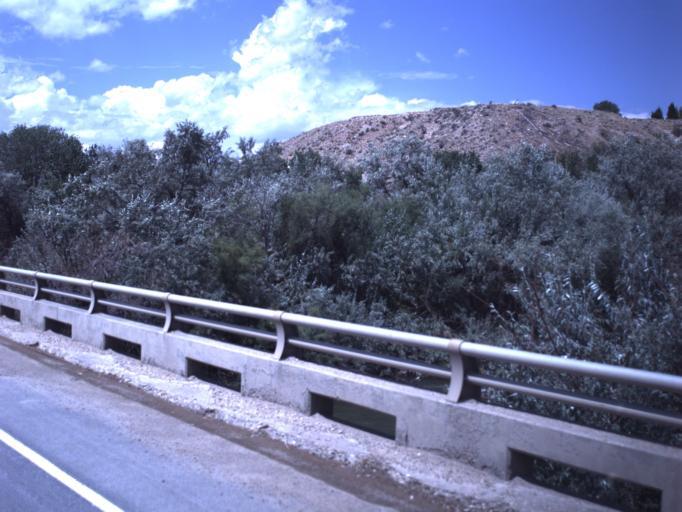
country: US
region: Utah
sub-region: Duchesne County
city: Duchesne
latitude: 40.1610
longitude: -110.3883
